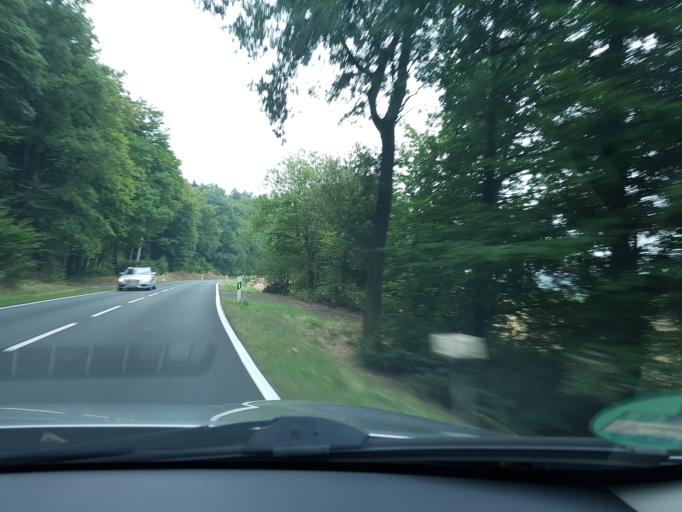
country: DE
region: Rheinland-Pfalz
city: Becheln
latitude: 50.3000
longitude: 7.7153
